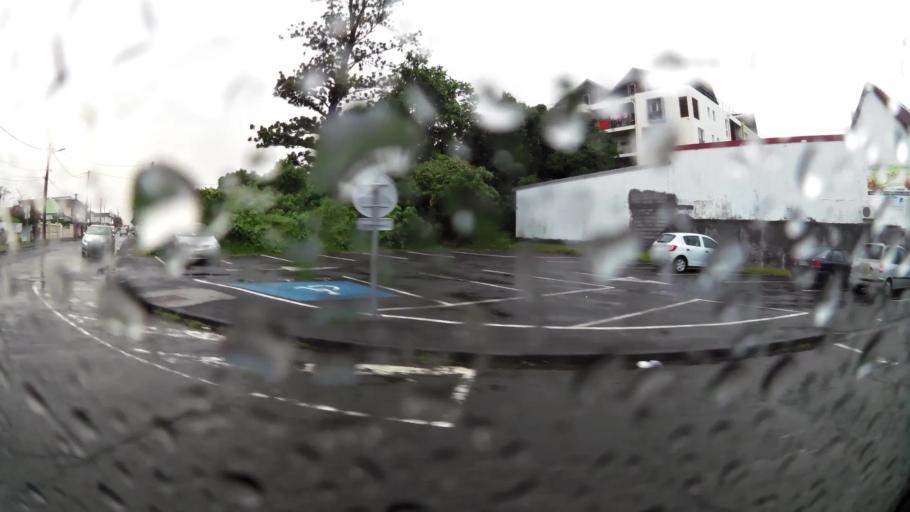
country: RE
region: Reunion
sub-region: Reunion
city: Saint-Benoit
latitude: -21.0356
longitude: 55.7172
